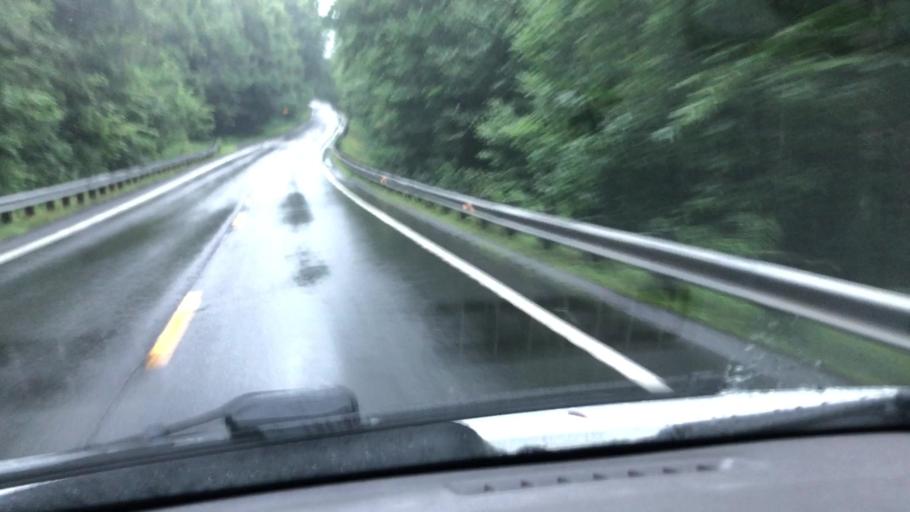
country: US
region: Massachusetts
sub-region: Hampshire County
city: Chesterfield
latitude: 42.3103
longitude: -72.8627
